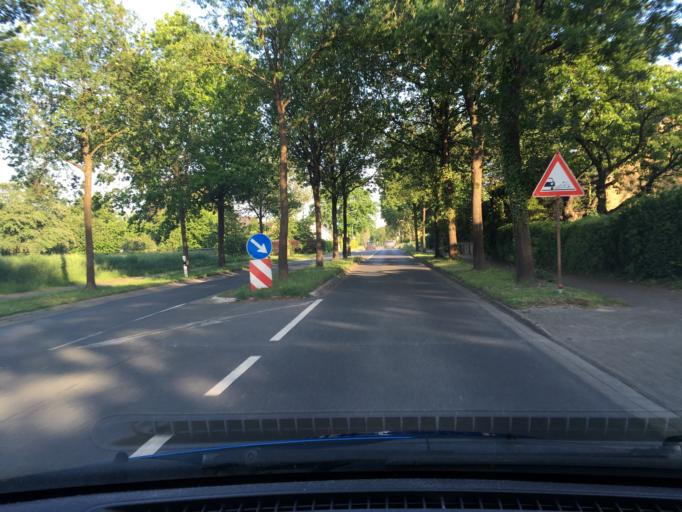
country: DE
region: Lower Saxony
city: Otter
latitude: 53.2614
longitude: 9.7375
